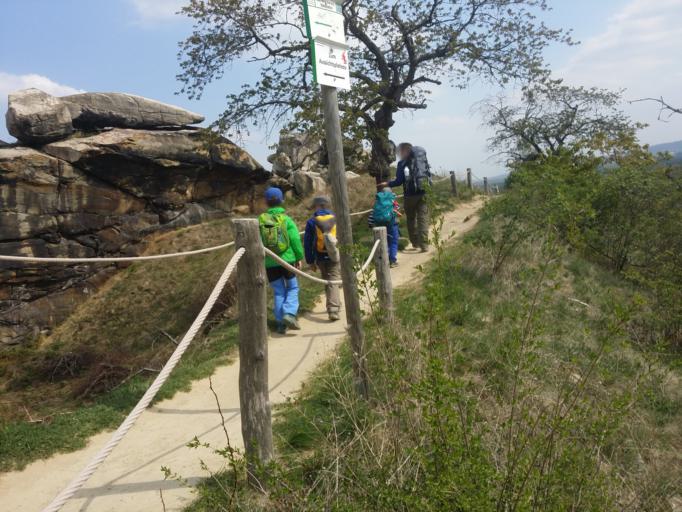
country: DE
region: Saxony-Anhalt
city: Weddersleben
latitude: 51.7572
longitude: 11.0844
